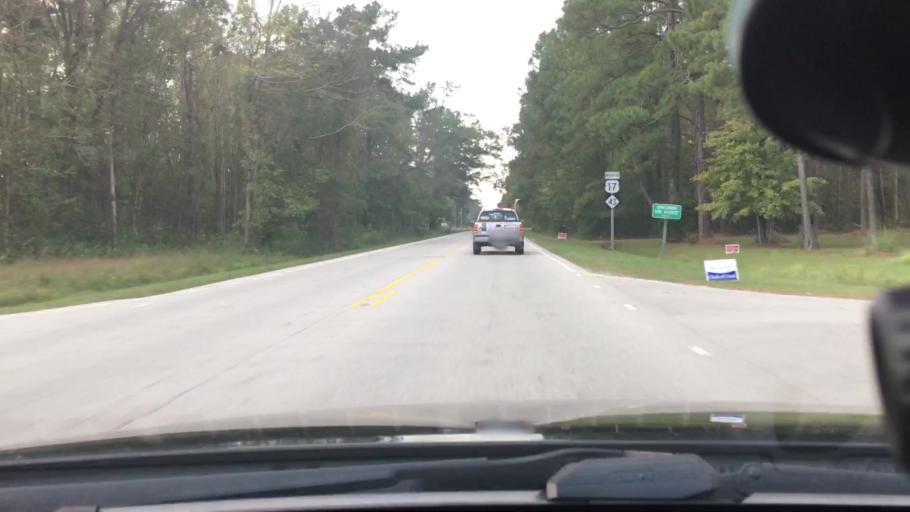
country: US
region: North Carolina
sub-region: Craven County
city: Vanceboro
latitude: 35.2625
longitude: -77.1028
